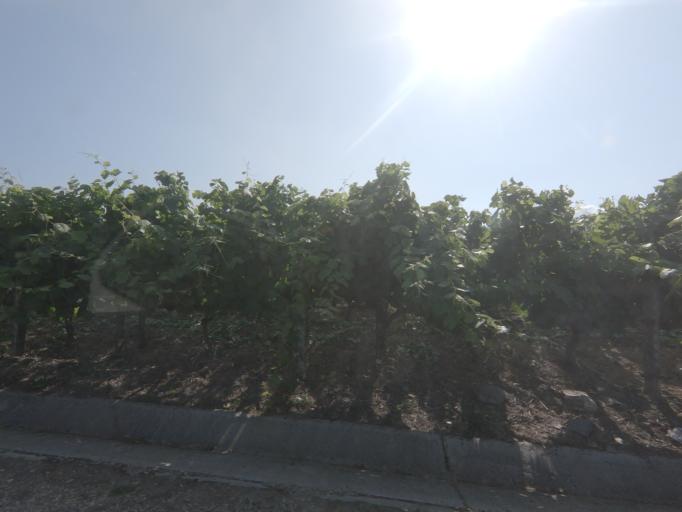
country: PT
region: Vila Real
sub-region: Sabrosa
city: Sabrosa
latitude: 41.2612
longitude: -7.5780
